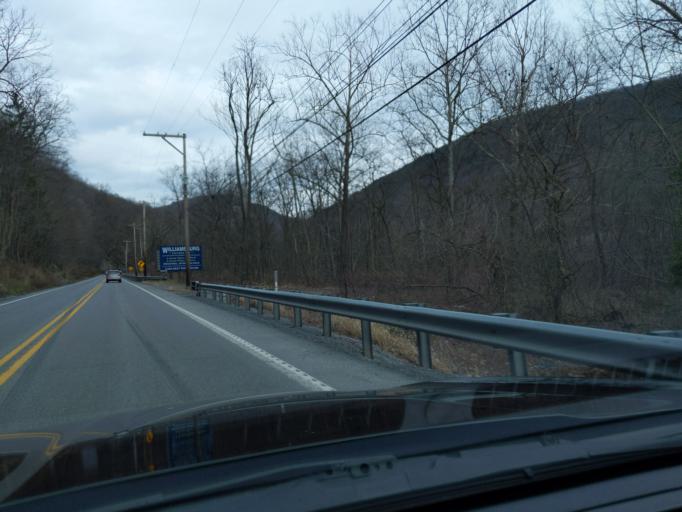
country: US
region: Pennsylvania
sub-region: Blair County
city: Williamsburg
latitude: 40.4829
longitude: -78.2569
